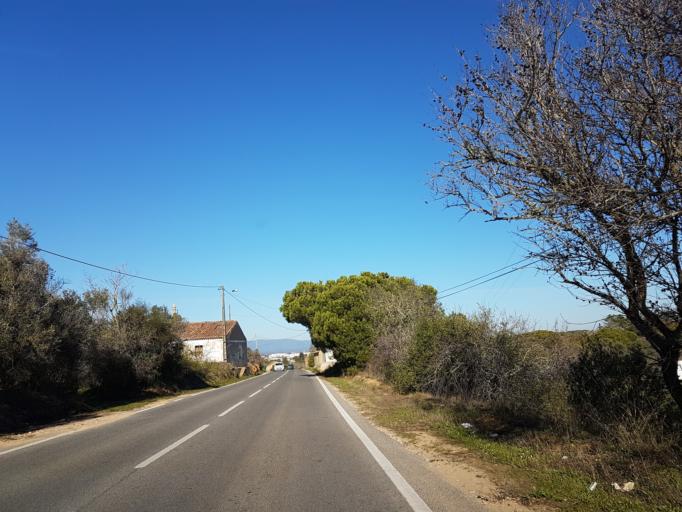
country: PT
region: Faro
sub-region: Lagoa
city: Carvoeiro
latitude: 37.1027
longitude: -8.4442
